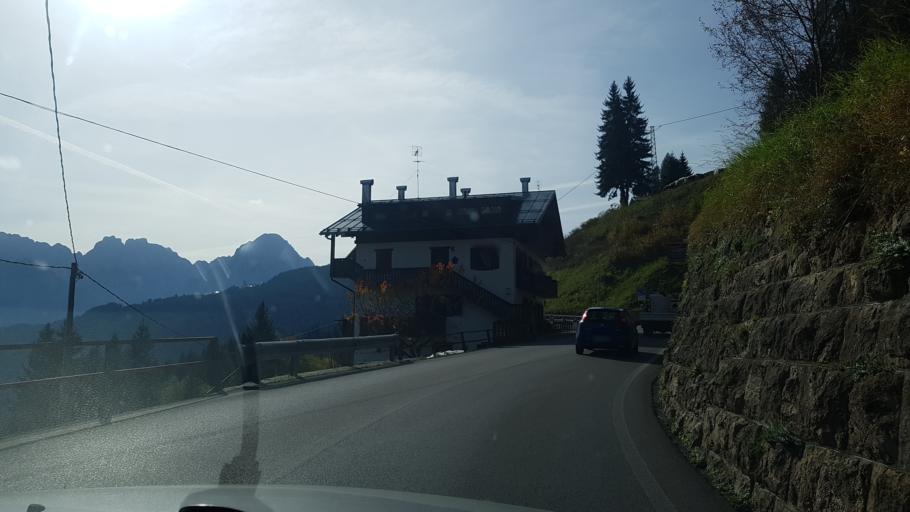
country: IT
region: Veneto
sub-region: Provincia di Belluno
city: Candide
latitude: 46.5932
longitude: 12.5196
